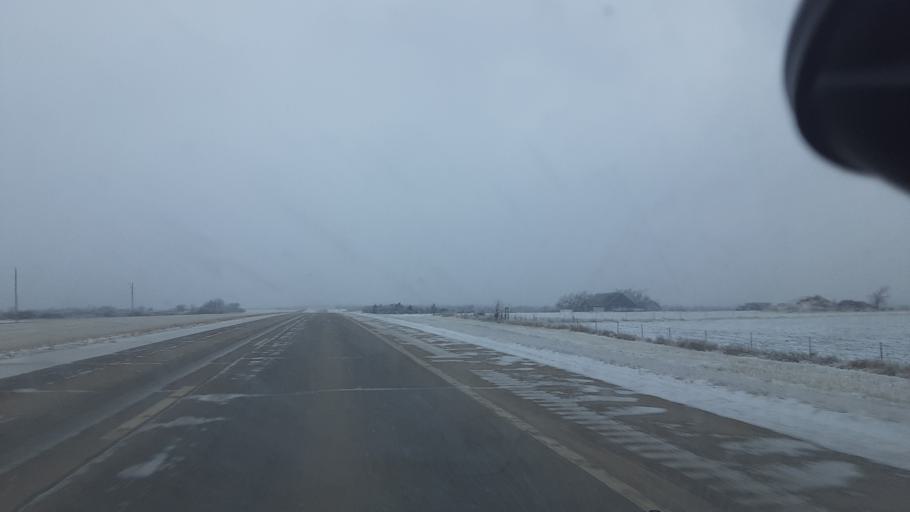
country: US
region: Oklahoma
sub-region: Logan County
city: Langston
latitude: 35.9223
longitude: -97.3240
